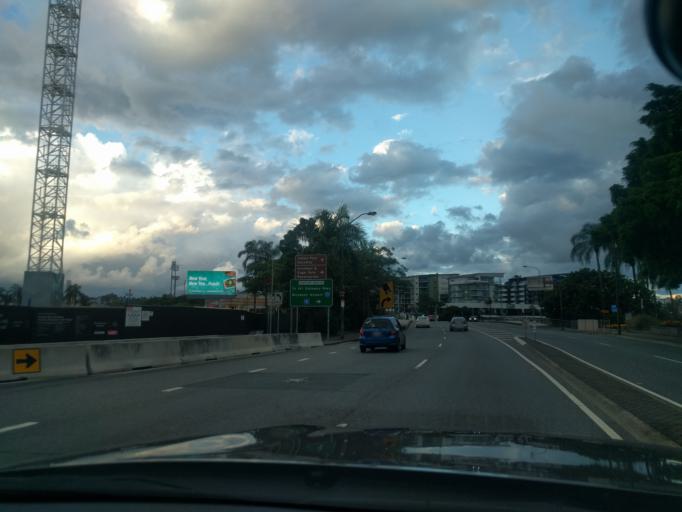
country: AU
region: Queensland
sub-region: Brisbane
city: Ascot
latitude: -27.4422
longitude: 153.0448
